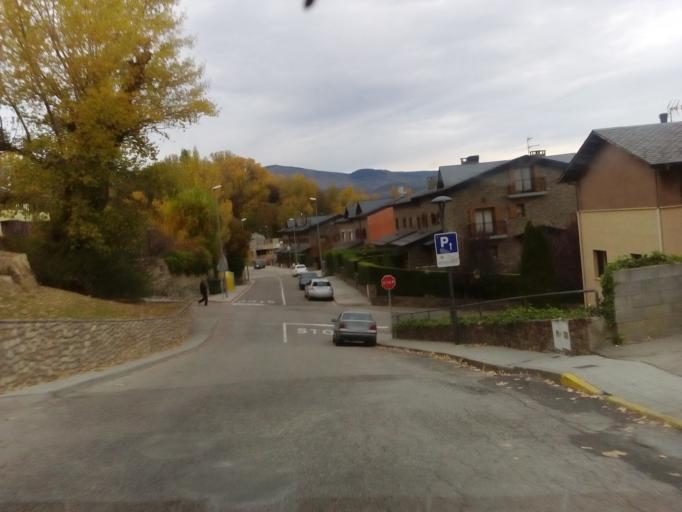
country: ES
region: Catalonia
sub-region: Provincia de Girona
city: Puigcerda
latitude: 42.4323
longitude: 1.9312
